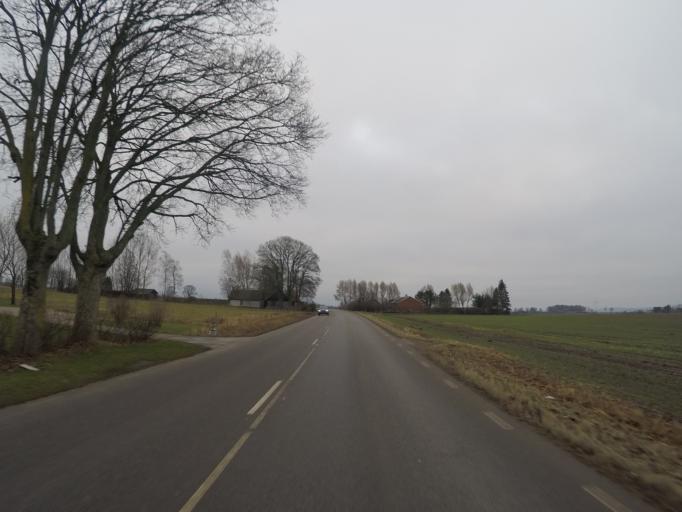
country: SE
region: Skane
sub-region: Hoors Kommun
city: Loberod
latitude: 55.7762
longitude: 13.4298
